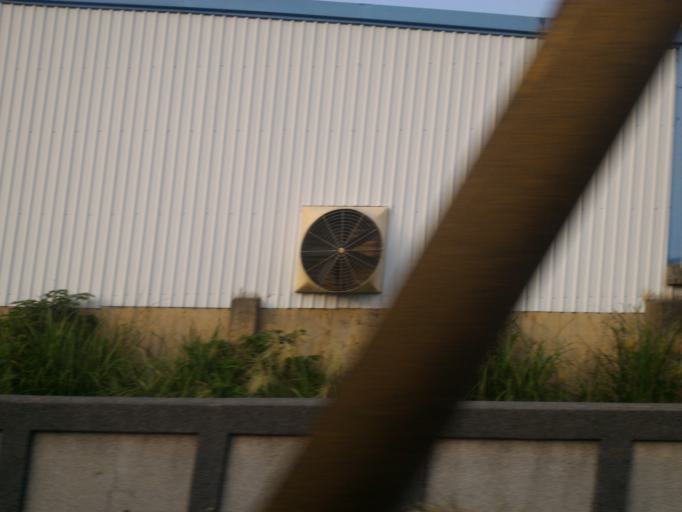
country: TW
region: Taiwan
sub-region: Taoyuan
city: Taoyuan
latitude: 24.9482
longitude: 121.3397
